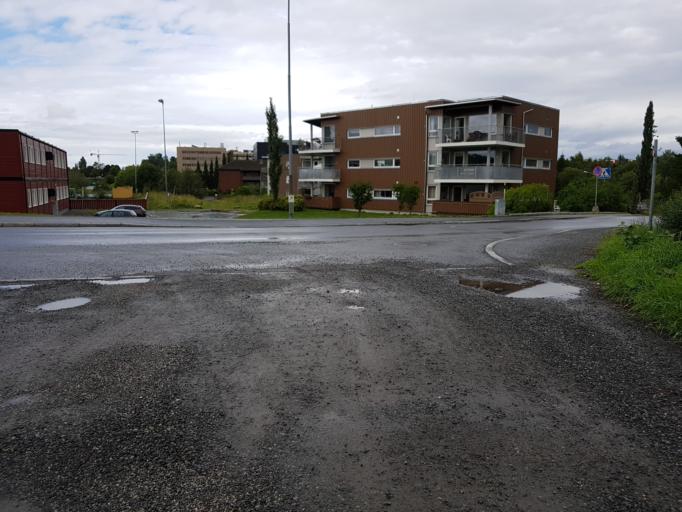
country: NO
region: Sor-Trondelag
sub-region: Trondheim
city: Trondheim
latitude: 63.3983
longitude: 10.4085
